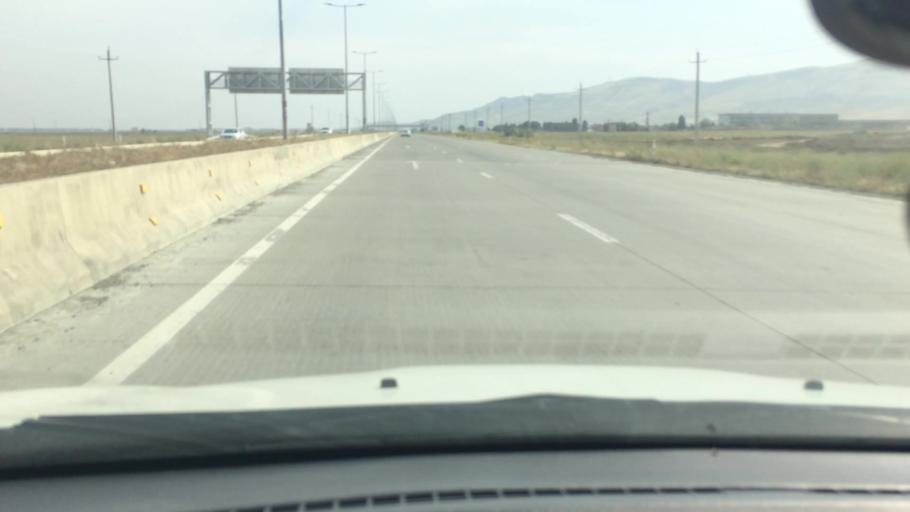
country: GE
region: Kvemo Kartli
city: Rust'avi
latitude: 41.5997
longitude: 44.9411
